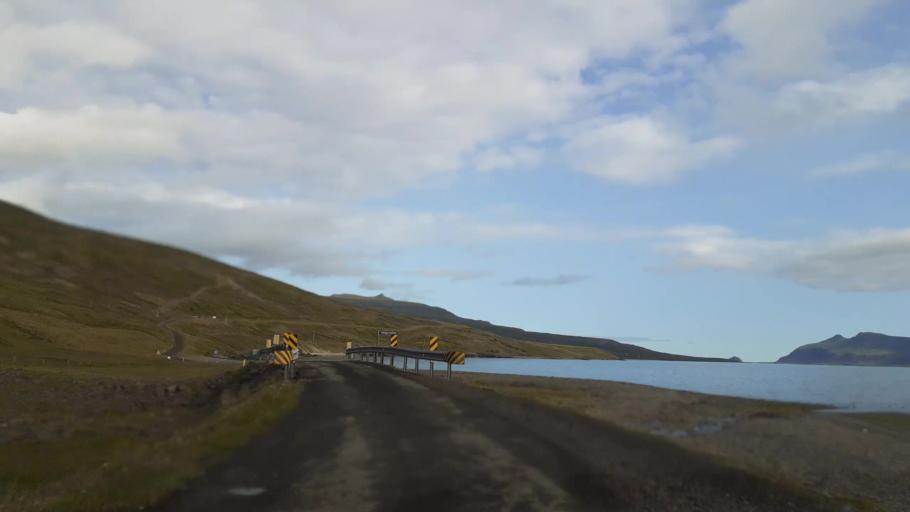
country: IS
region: East
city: Eskifjoerdur
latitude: 65.0354
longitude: -13.8738
